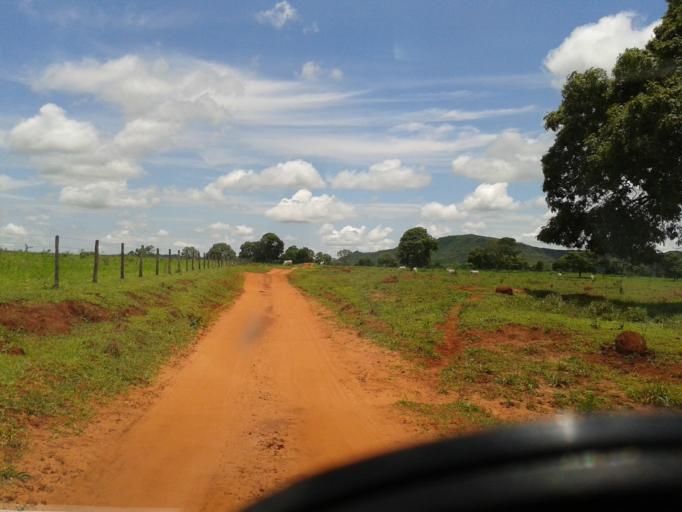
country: BR
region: Minas Gerais
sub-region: Santa Vitoria
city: Santa Vitoria
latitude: -18.9985
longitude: -49.9145
